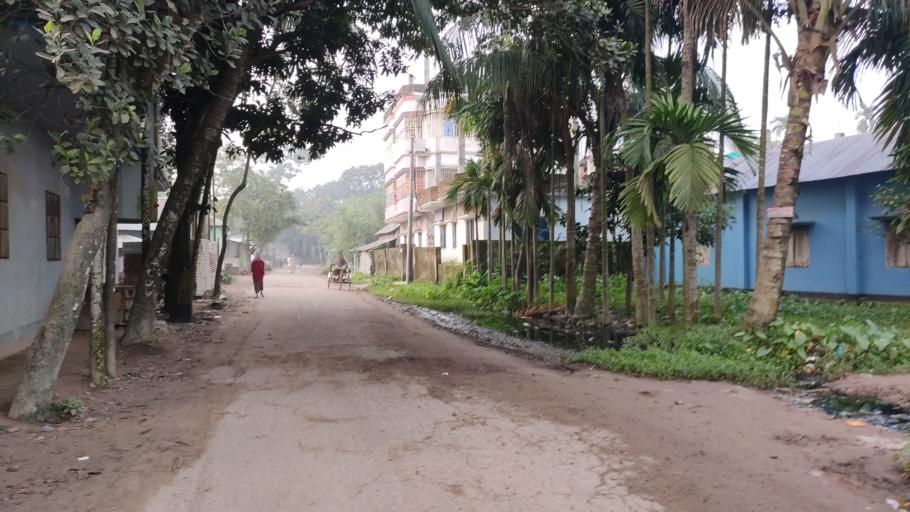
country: BD
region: Dhaka
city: Netrakona
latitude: 24.7141
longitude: 90.9468
